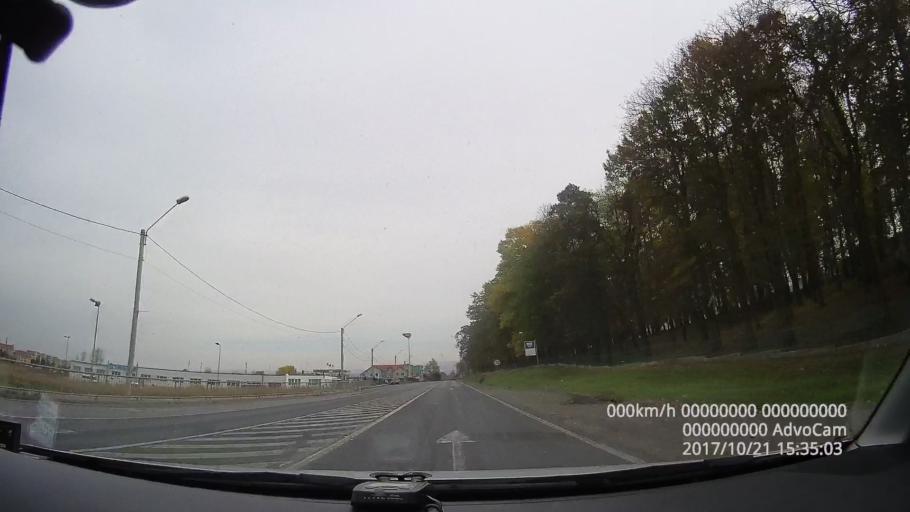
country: RO
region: Hunedoara
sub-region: Comuna Soimus
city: Soimus
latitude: 45.9126
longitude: 22.8594
